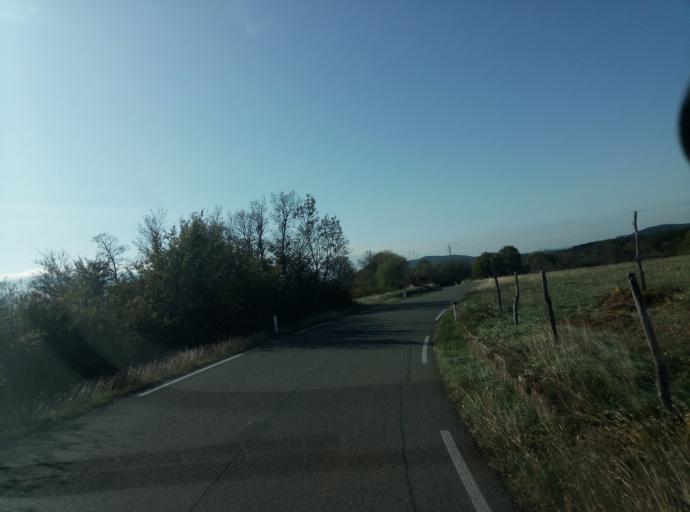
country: SI
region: Komen
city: Komen
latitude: 45.8066
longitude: 13.7233
